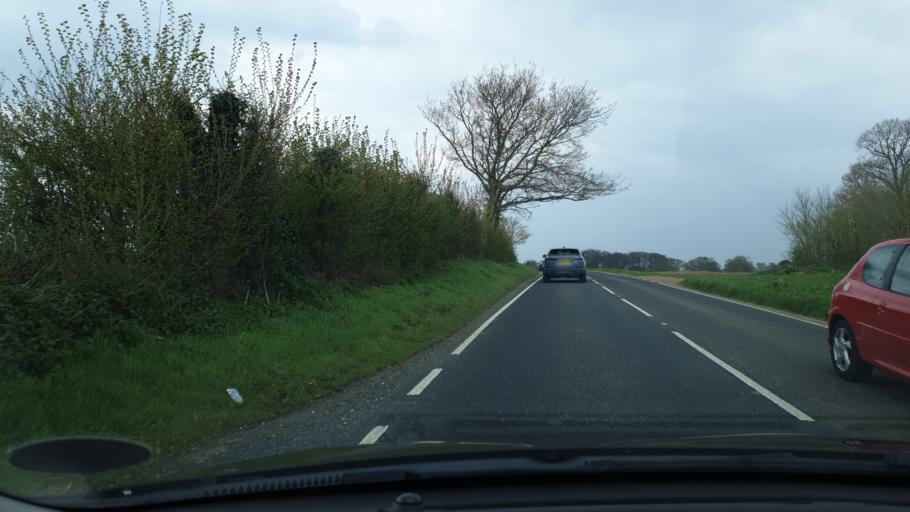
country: GB
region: England
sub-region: Essex
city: Mistley
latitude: 51.9335
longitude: 1.0738
